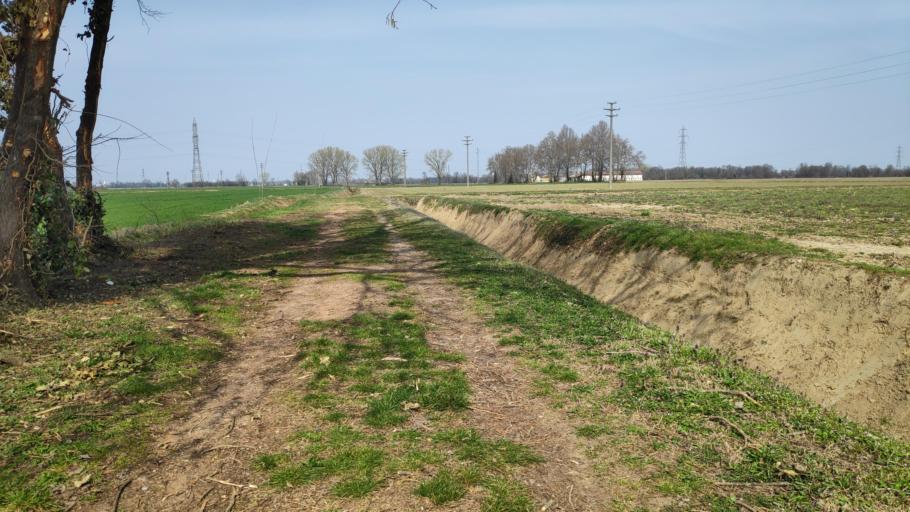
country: IT
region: Lombardy
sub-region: Citta metropolitana di Milano
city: Pantigliate
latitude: 45.4434
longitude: 9.3648
